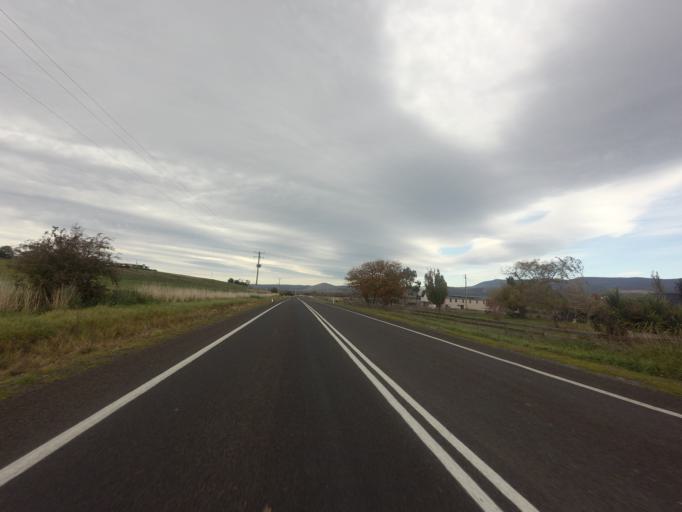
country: AU
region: Tasmania
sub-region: Derwent Valley
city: New Norfolk
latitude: -42.4948
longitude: 146.7292
